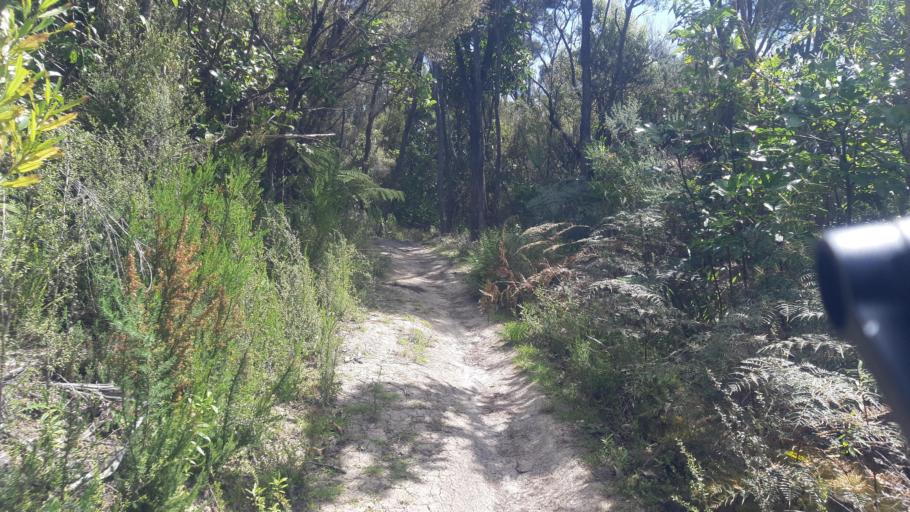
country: NZ
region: Marlborough
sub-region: Marlborough District
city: Picton
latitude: -41.2523
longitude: 174.0447
